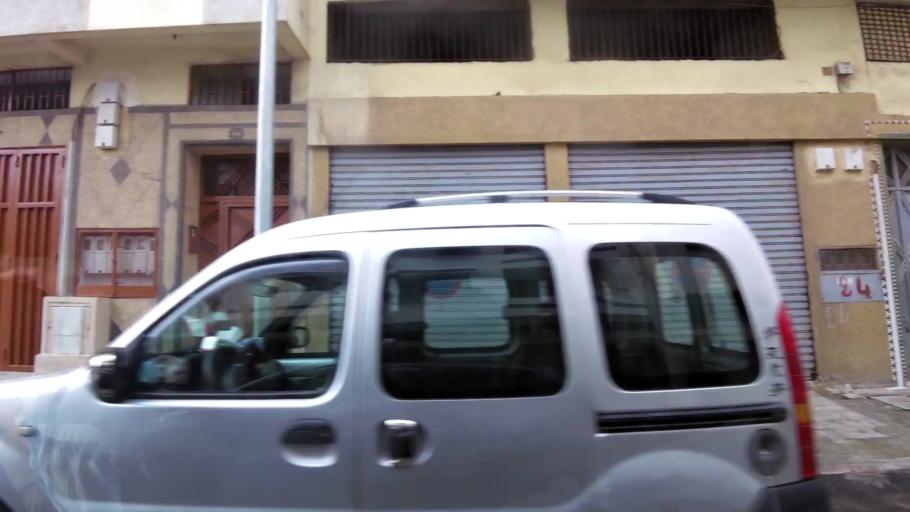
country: MA
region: Grand Casablanca
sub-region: Casablanca
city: Casablanca
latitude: 33.5652
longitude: -7.6736
